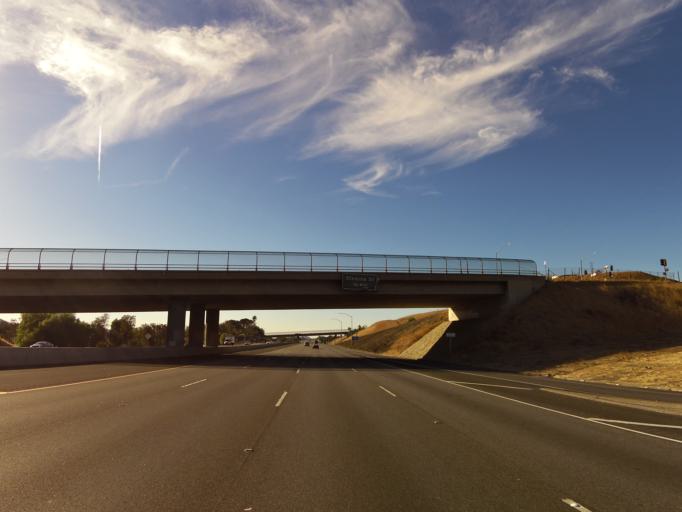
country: US
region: California
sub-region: Ventura County
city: Santa Susana
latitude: 34.2817
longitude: -118.6777
